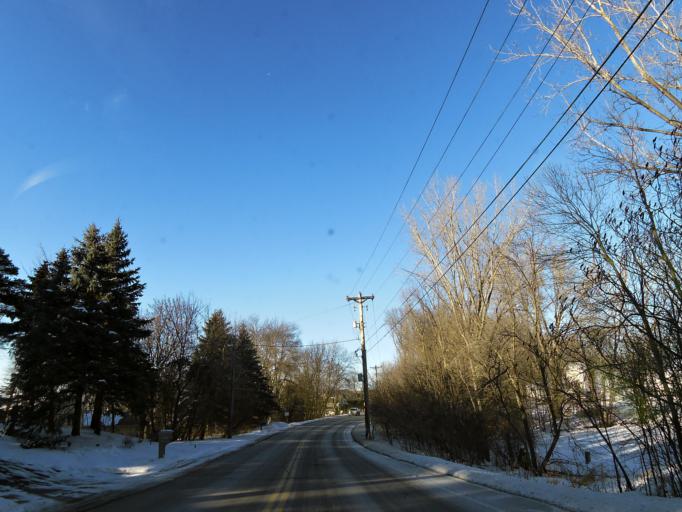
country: US
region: Minnesota
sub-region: Hennepin County
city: Mound
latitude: 44.9046
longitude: -93.6782
